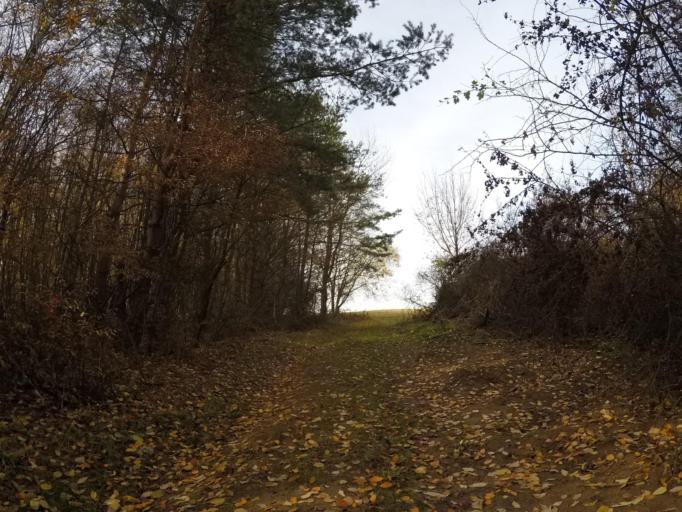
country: SK
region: Presovsky
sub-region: Okres Presov
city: Presov
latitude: 48.9216
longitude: 21.2248
